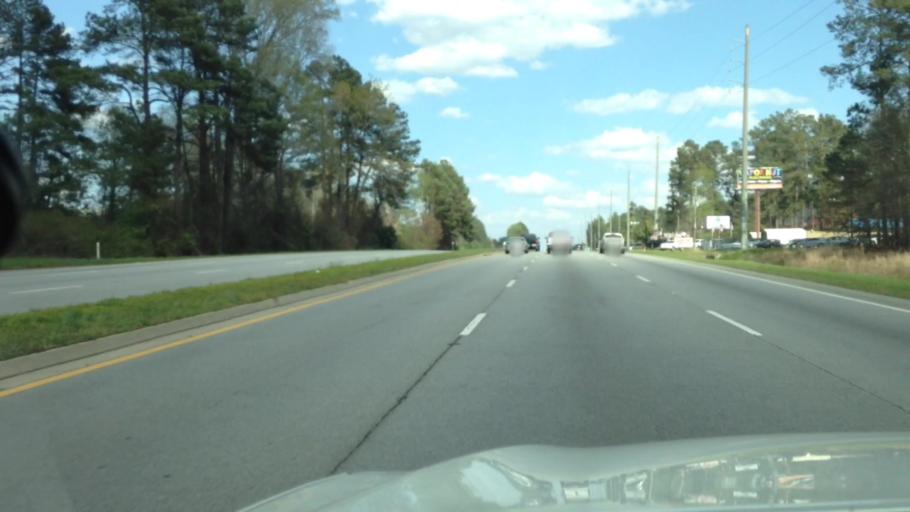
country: US
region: Georgia
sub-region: Columbia County
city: Martinez
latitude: 33.4424
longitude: -82.1012
